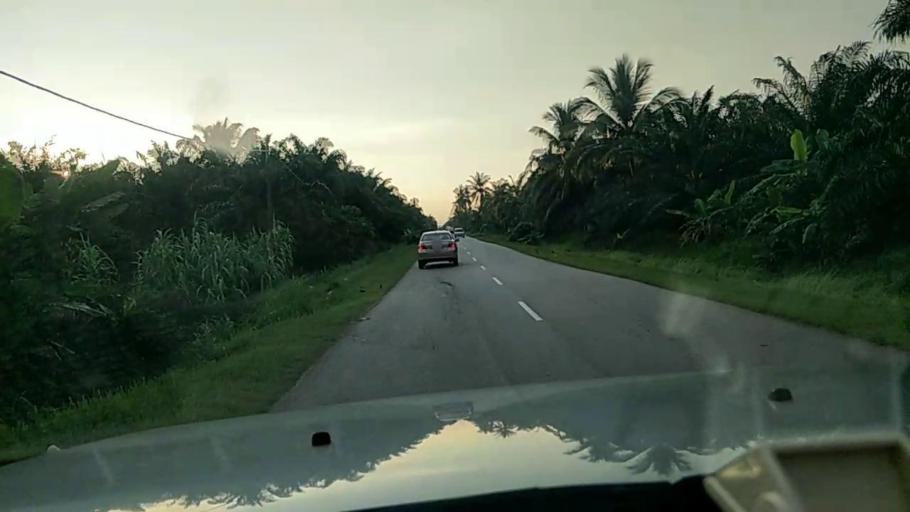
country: MY
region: Selangor
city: Kuala Selangor
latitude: 3.3132
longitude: 101.2853
